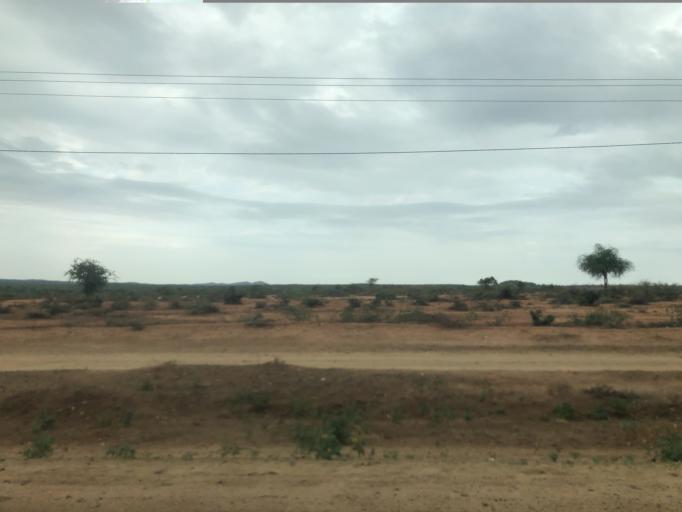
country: ET
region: Southern Nations, Nationalities, and People's Region
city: Turmi
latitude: 4.9728
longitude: 36.4857
